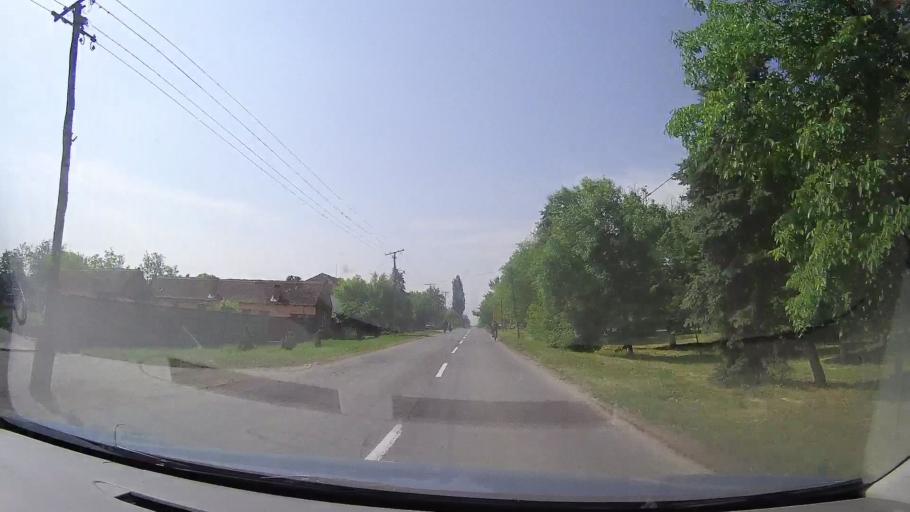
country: RS
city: Jarkovac
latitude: 45.2711
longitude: 20.7645
